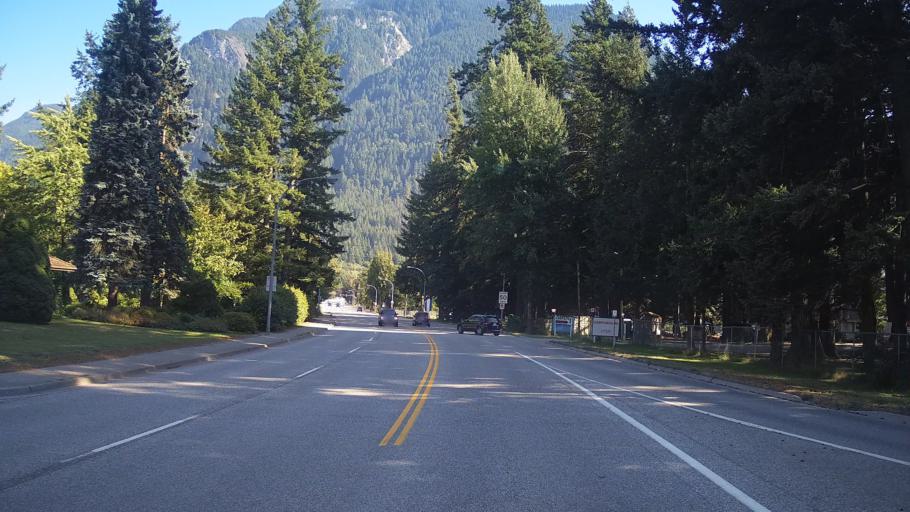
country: CA
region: British Columbia
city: Hope
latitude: 49.3824
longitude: -121.4475
